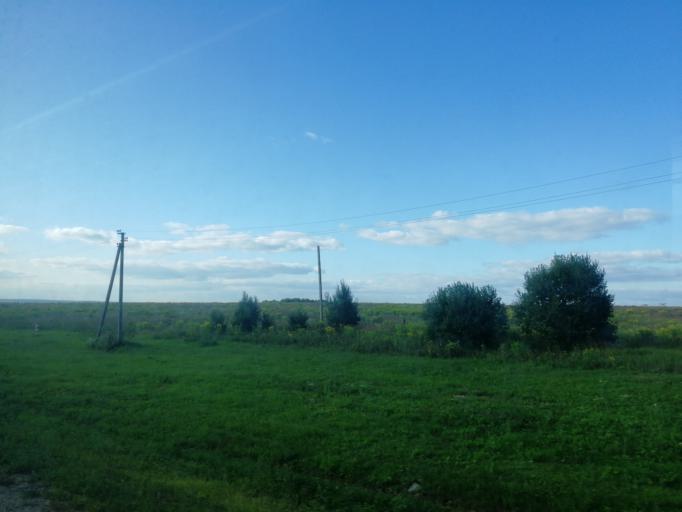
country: RU
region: Tula
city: Leninskiy
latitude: 54.2389
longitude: 37.3438
